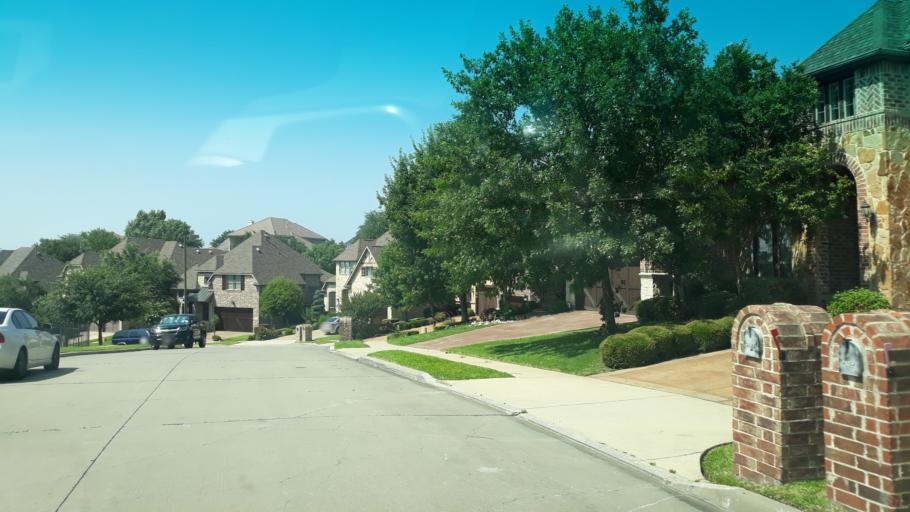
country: US
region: Texas
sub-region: Dallas County
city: Irving
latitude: 32.8578
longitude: -96.9723
